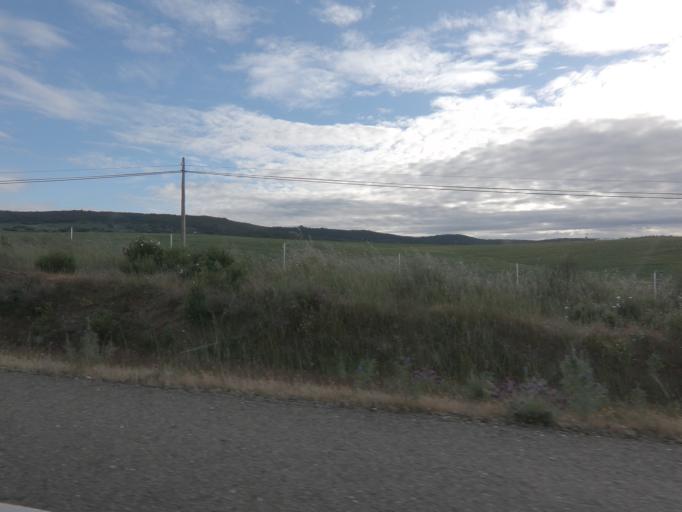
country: ES
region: Extremadura
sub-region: Provincia de Caceres
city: Pedroso de Acim
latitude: 39.8376
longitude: -6.3936
